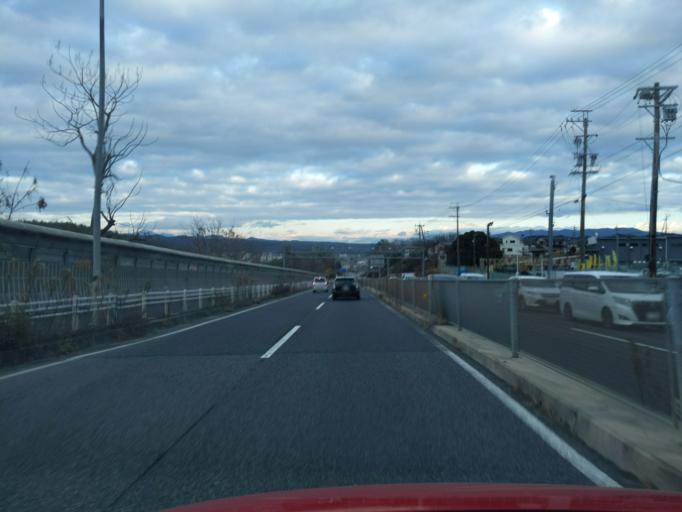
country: JP
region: Gifu
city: Toki
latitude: 35.3466
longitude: 137.1649
